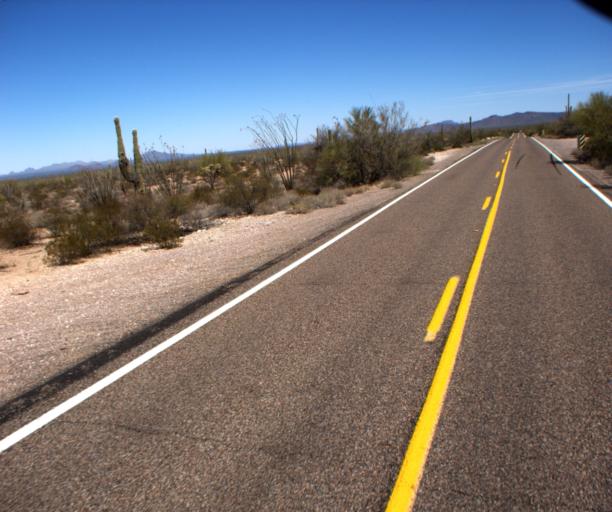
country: MX
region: Sonora
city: Sonoyta
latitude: 32.0930
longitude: -112.7741
